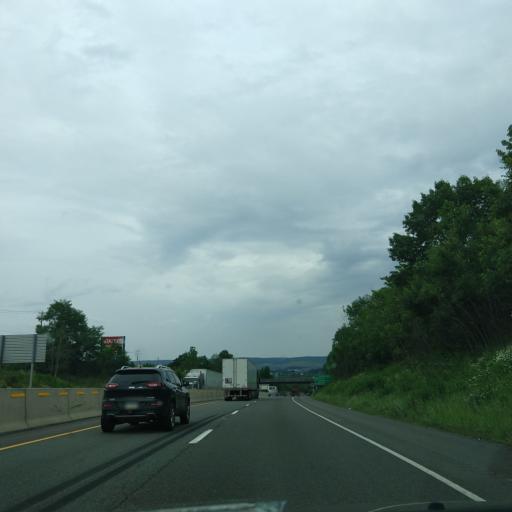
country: US
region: Pennsylvania
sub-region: Lackawanna County
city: Chinchilla
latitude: 41.4549
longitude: -75.6524
